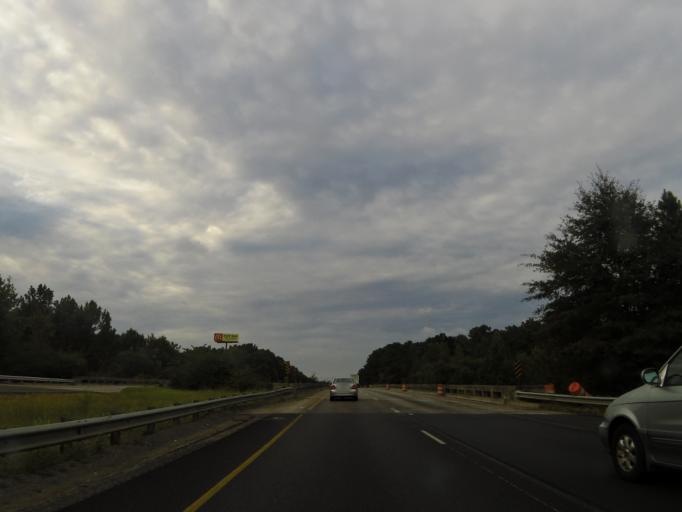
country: US
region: Alabama
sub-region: Shelby County
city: Pelham
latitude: 33.2637
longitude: -86.7990
